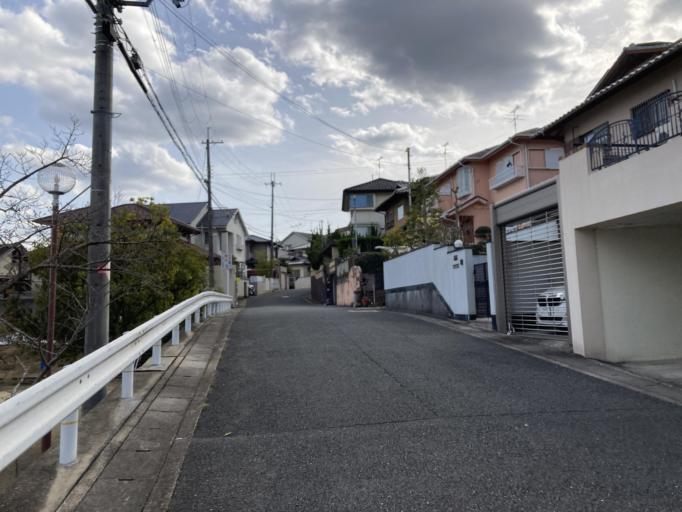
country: JP
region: Nara
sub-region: Ikoma-shi
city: Ikoma
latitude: 34.7119
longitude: 135.6918
